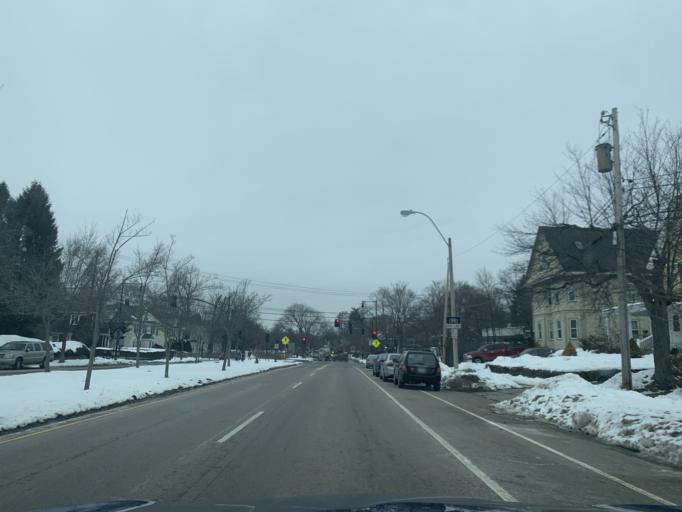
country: US
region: Massachusetts
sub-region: Norfolk County
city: Milton
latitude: 42.2616
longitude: -71.0935
